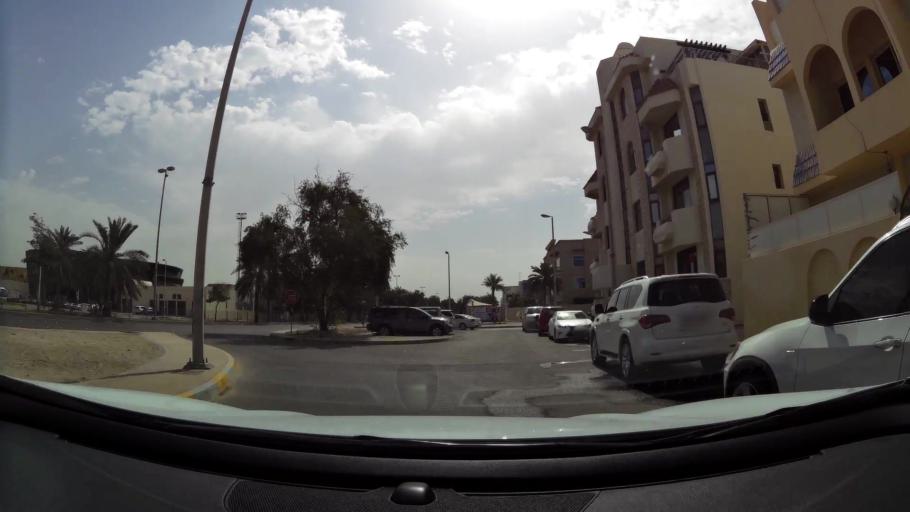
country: AE
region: Abu Dhabi
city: Abu Dhabi
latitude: 24.4578
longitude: 54.3593
